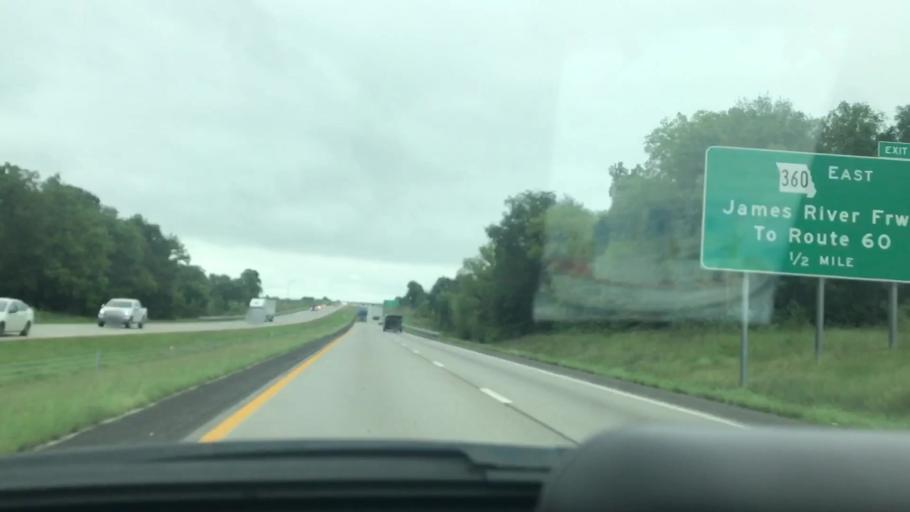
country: US
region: Missouri
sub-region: Greene County
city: Republic
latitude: 37.1934
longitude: -93.4570
